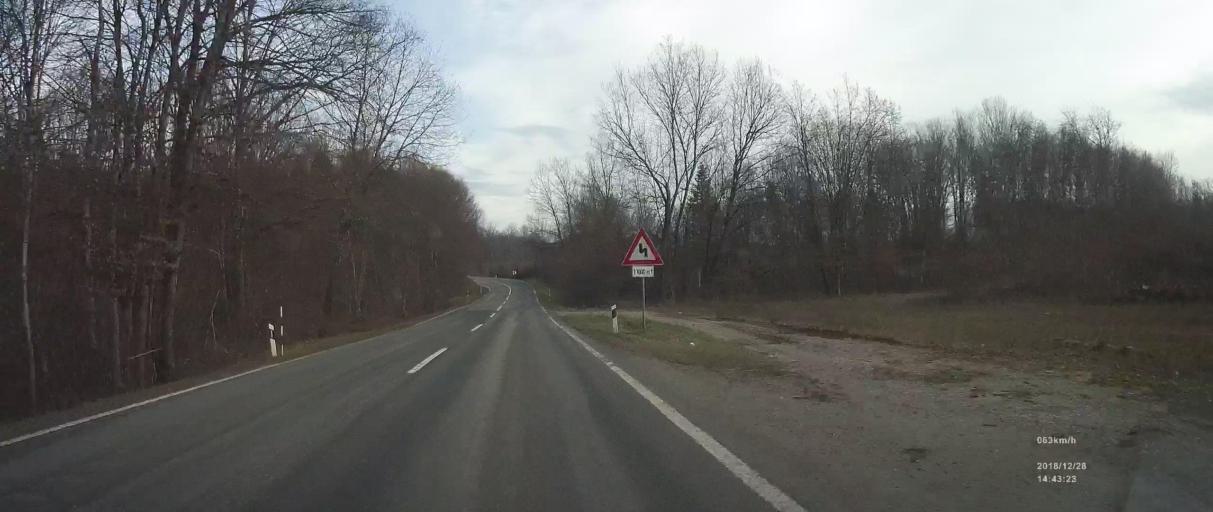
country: SI
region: Crnomelj
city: Crnomelj
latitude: 45.4466
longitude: 15.2780
